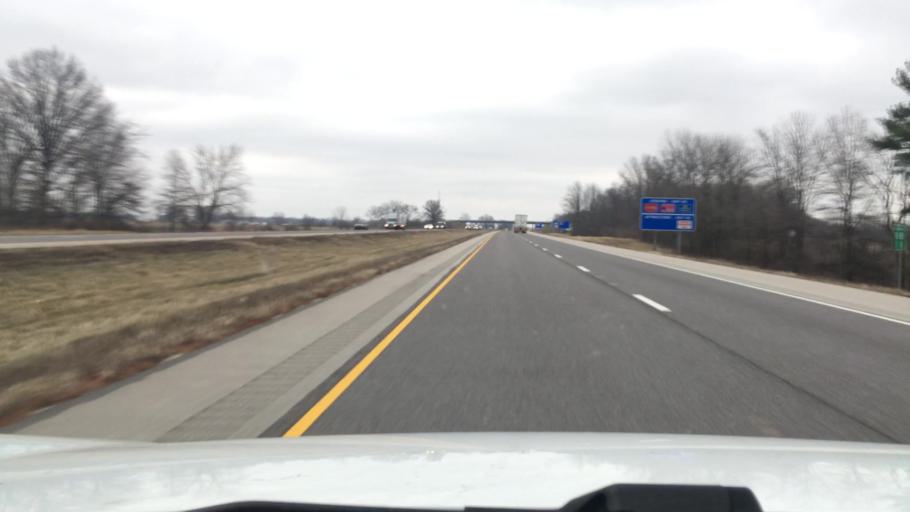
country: US
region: Illinois
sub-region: Effingham County
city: Altamont
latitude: 39.0365
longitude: -88.7740
